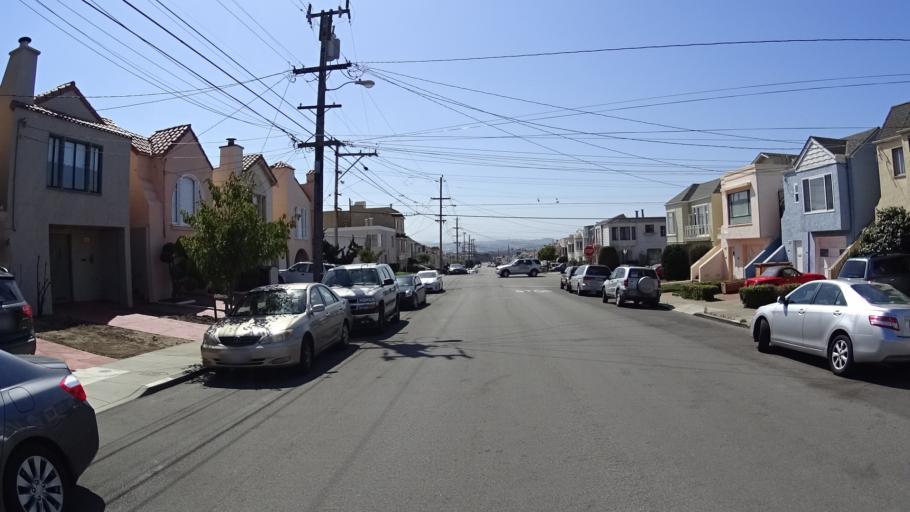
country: US
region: California
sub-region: San Mateo County
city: Daly City
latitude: 37.7466
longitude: -122.4888
